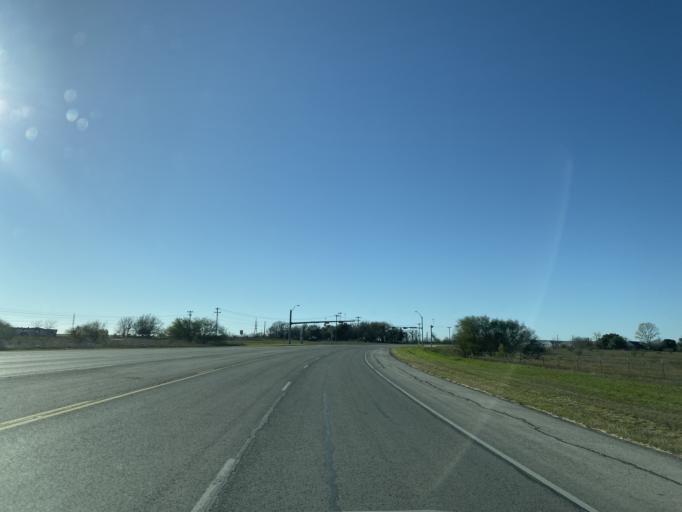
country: US
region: Texas
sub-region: Guadalupe County
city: Redwood
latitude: 29.8280
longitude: -97.9557
